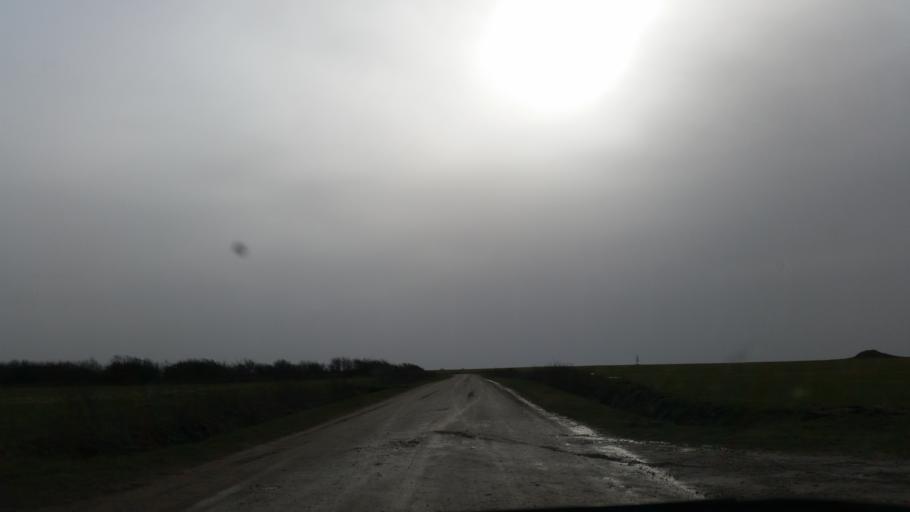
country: DE
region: Schleswig-Holstein
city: Klanxbull
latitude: 54.9970
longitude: 8.6603
